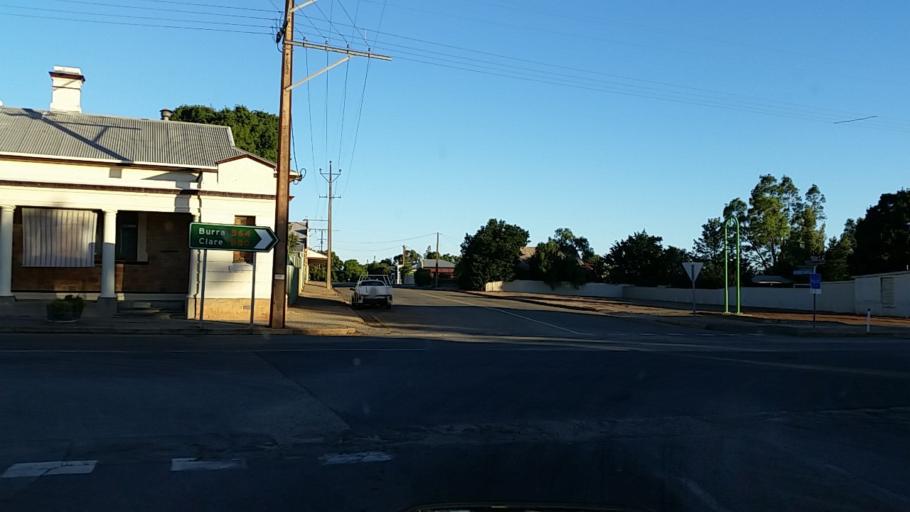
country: AU
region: South Australia
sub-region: Northern Areas
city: Jamestown
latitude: -33.4989
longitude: 138.6075
